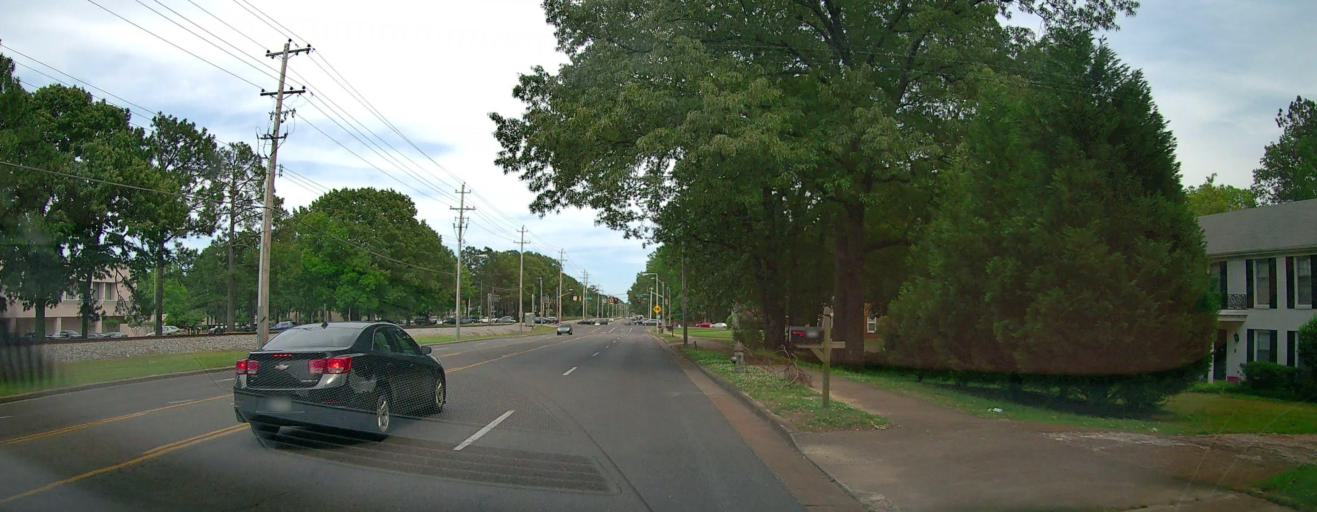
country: US
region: Tennessee
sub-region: Shelby County
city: Germantown
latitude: 35.0961
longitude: -89.8421
